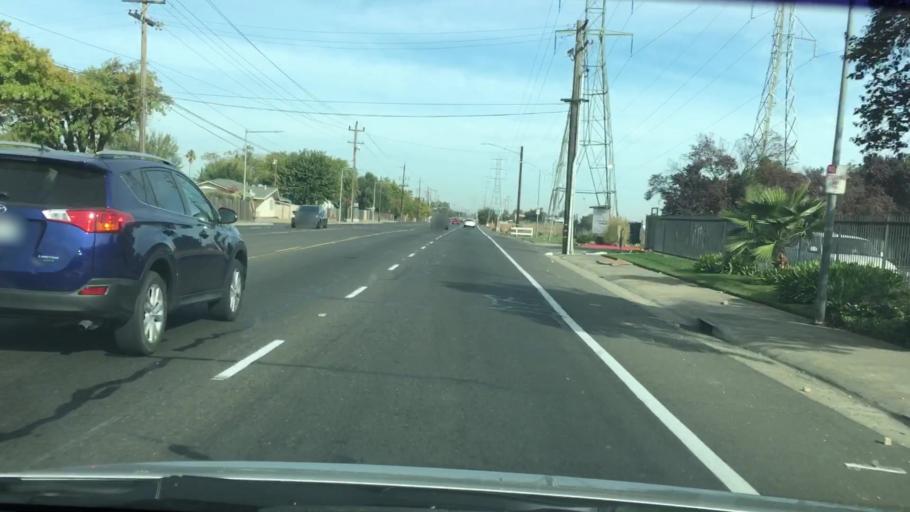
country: US
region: California
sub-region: Sacramento County
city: Florin
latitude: 38.4912
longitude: -121.4088
